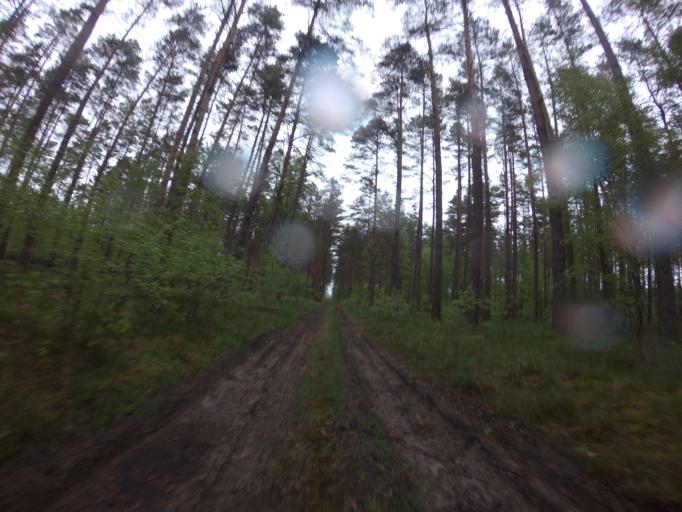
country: PL
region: West Pomeranian Voivodeship
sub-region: Powiat drawski
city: Kalisz Pomorski
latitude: 53.2254
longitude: 16.0131
